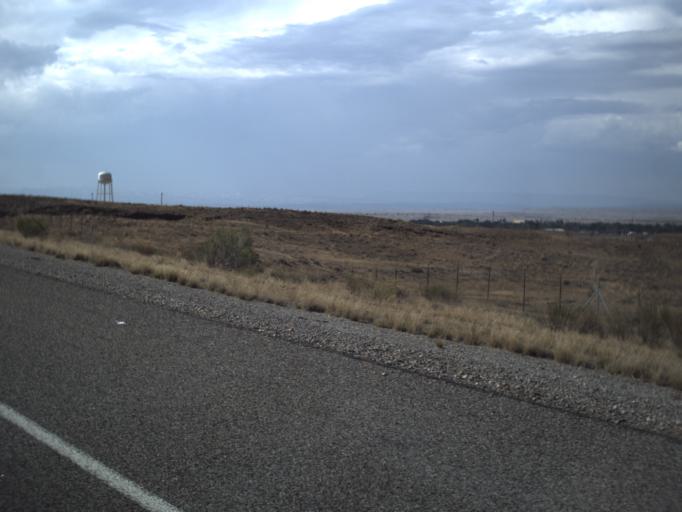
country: US
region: Utah
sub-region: Carbon County
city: East Carbon City
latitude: 38.9763
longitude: -110.1262
